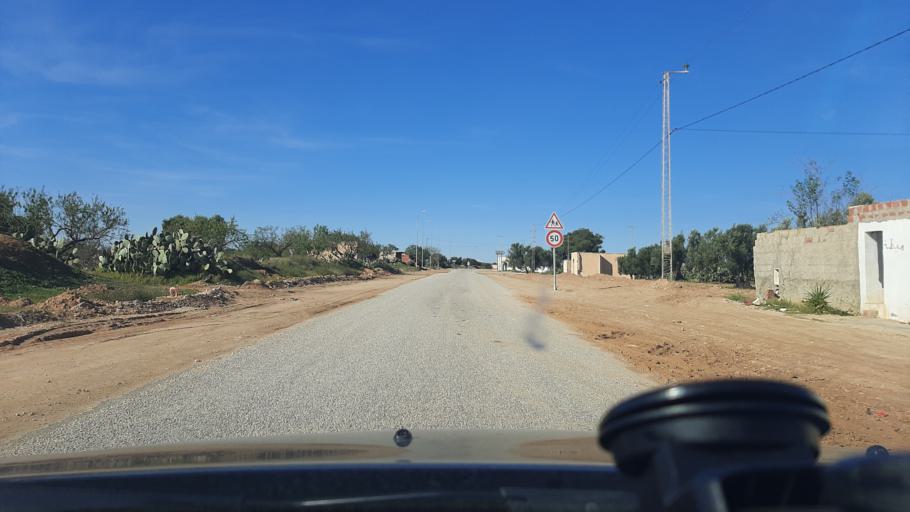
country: TN
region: Safaqis
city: Sfax
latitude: 34.9085
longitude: 10.5940
